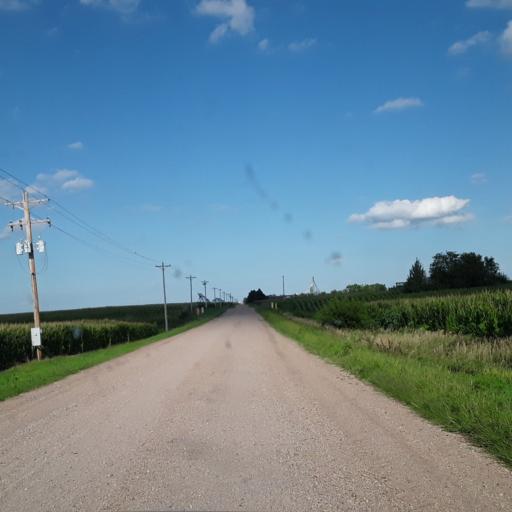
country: US
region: Nebraska
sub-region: Hall County
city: Wood River
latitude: 40.9167
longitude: -98.5629
